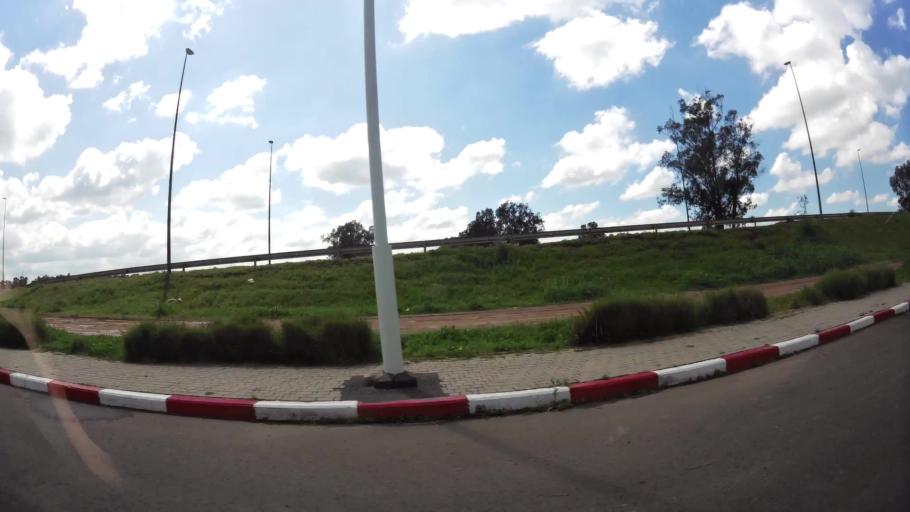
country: MA
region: Chaouia-Ouardigha
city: Nouaseur
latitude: 33.3760
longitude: -7.5681
